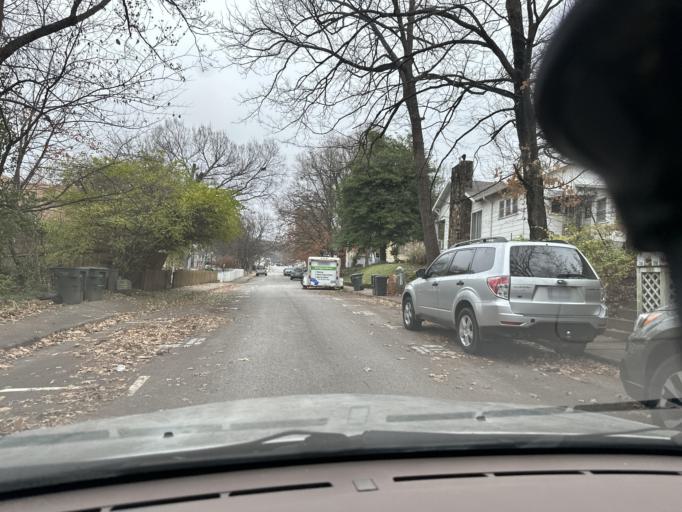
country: US
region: Arkansas
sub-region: Washington County
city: Fayetteville
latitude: 36.0637
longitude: -94.1636
